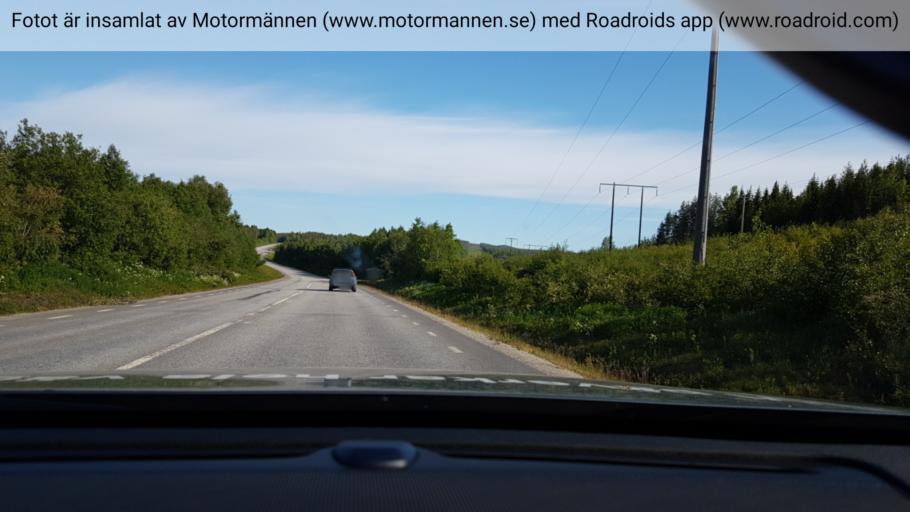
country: SE
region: Vaesterbotten
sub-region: Vannas Kommun
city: Vaennaes
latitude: 63.9920
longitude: 19.7320
